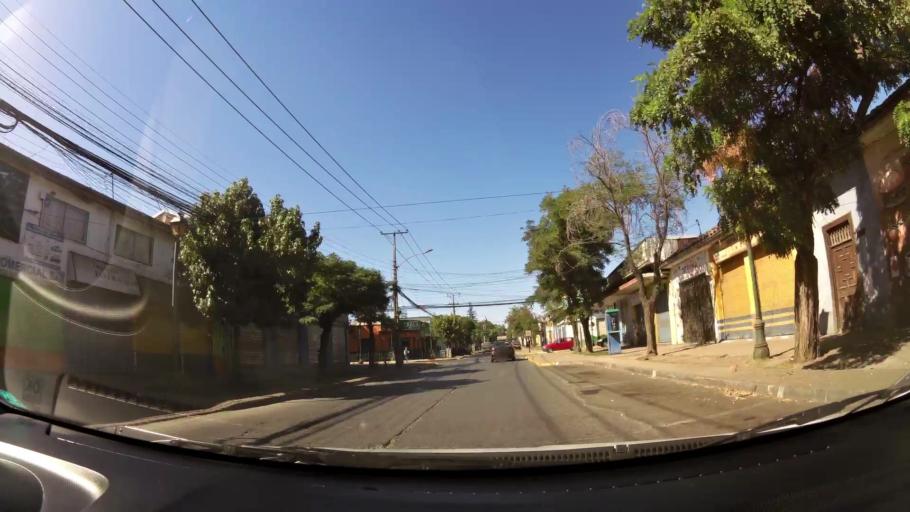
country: CL
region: O'Higgins
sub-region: Provincia de Cachapoal
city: Rancagua
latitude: -34.1710
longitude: -70.7490
